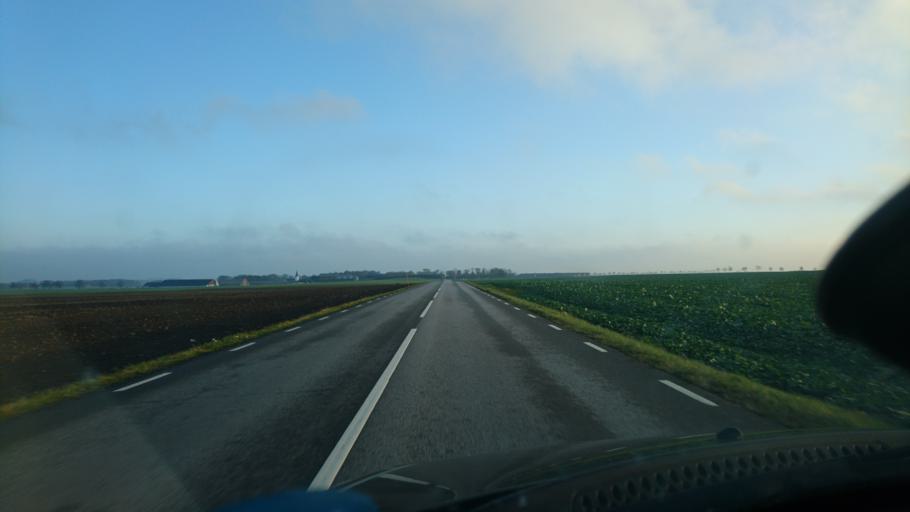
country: SE
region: Skane
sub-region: Tomelilla Kommun
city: Tomelilla
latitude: 55.4998
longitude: 14.0348
